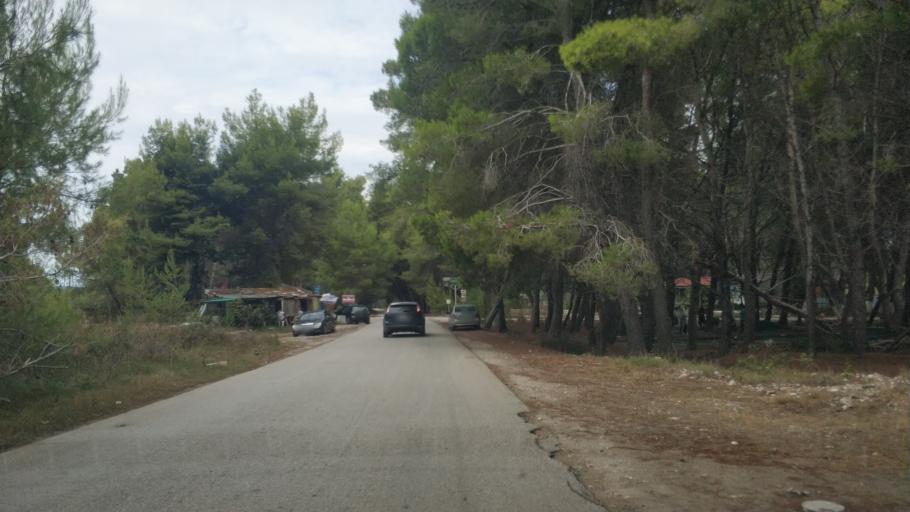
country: AL
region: Vlore
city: Vlore
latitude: 40.4883
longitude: 19.4421
